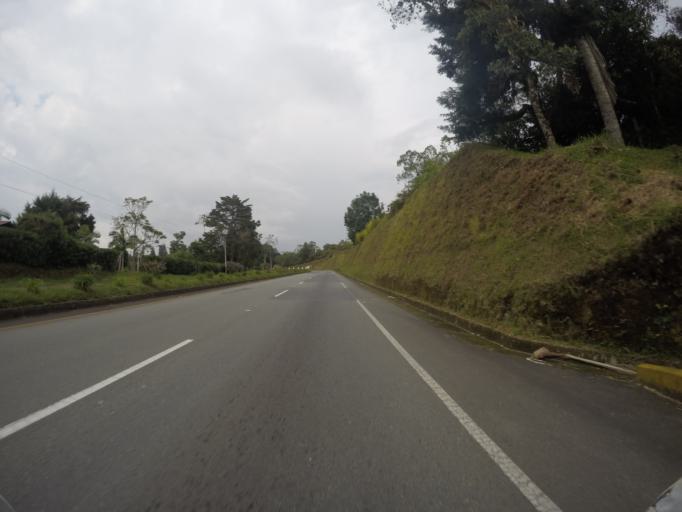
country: CO
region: Quindio
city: Filandia
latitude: 4.7372
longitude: -75.6489
